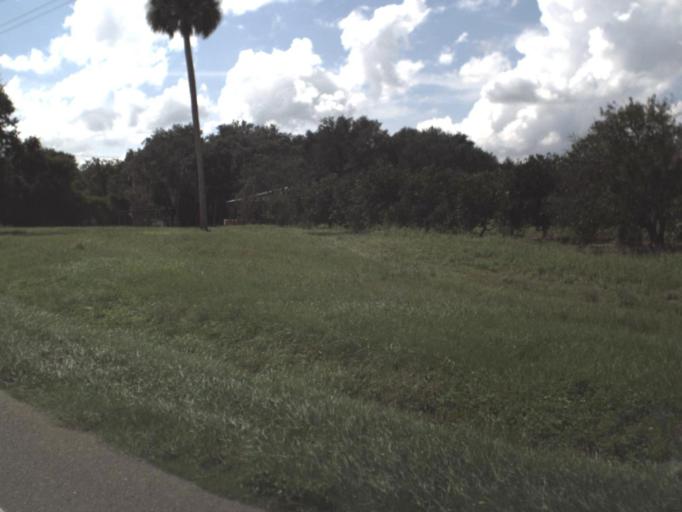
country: US
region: Florida
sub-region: Hardee County
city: Zolfo Springs
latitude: 27.4884
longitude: -81.8439
